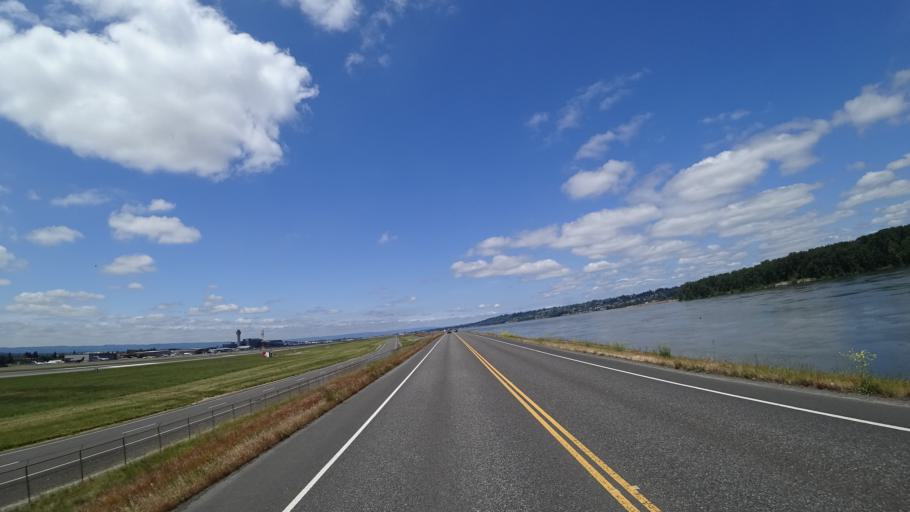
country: US
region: Washington
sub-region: Clark County
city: Orchards
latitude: 45.5860
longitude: -122.5684
